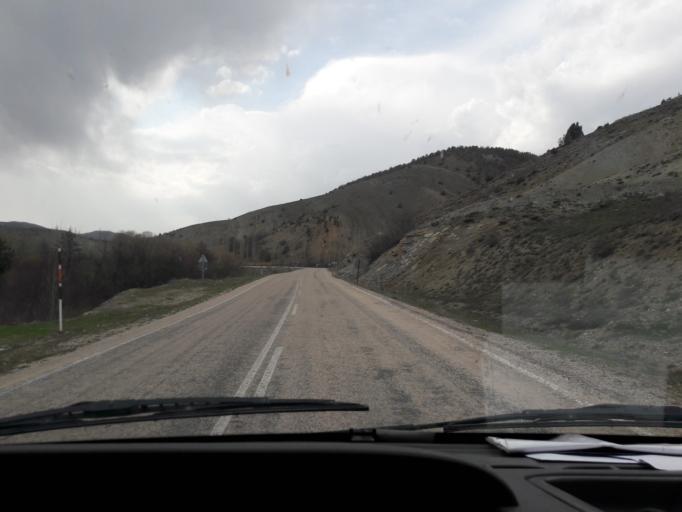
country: TR
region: Giresun
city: Alucra
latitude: 40.2881
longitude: 38.8188
